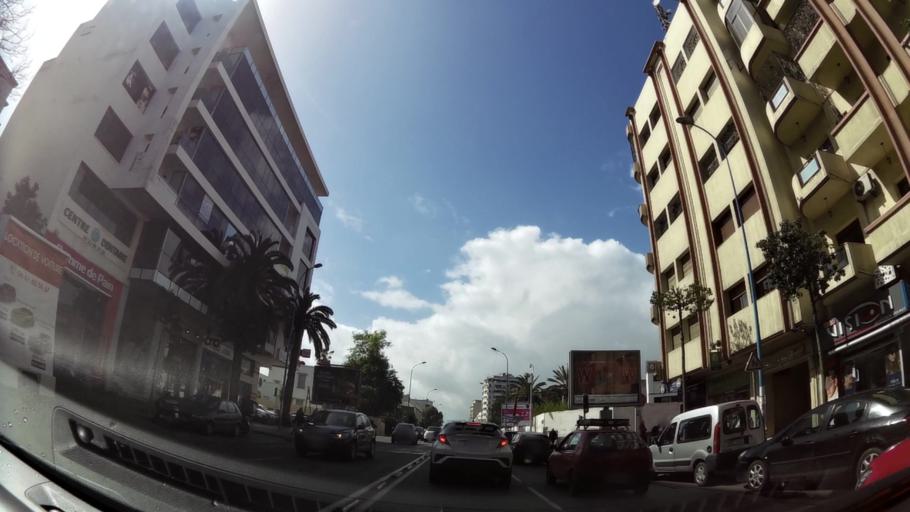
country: MA
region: Grand Casablanca
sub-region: Casablanca
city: Casablanca
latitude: 33.5790
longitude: -7.6152
